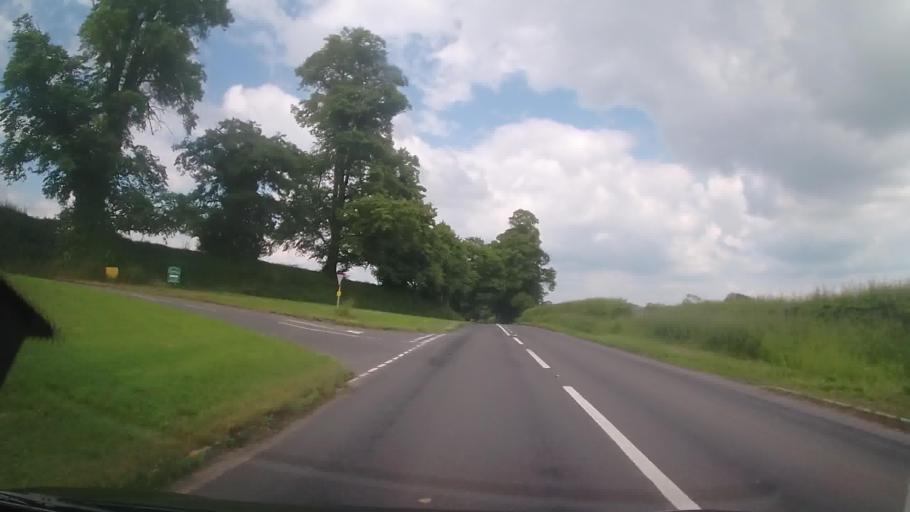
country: GB
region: England
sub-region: Shropshire
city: Ellesmere
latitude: 52.9007
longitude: -2.9158
